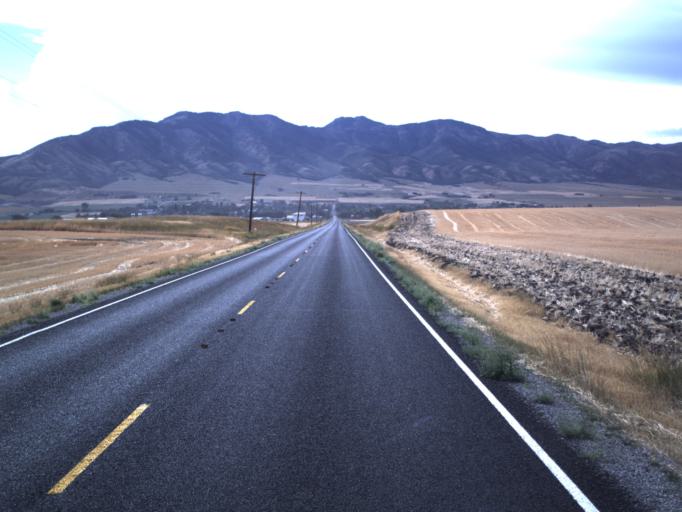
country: US
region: Utah
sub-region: Cache County
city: Benson
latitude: 41.9193
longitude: -112.0146
